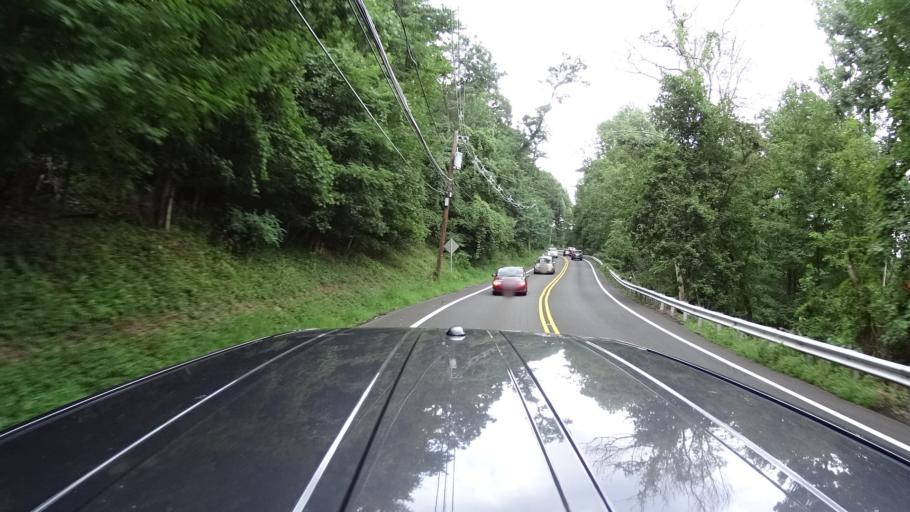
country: US
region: New Jersey
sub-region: Middlesex County
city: Dunellen
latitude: 40.6012
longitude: -74.4900
